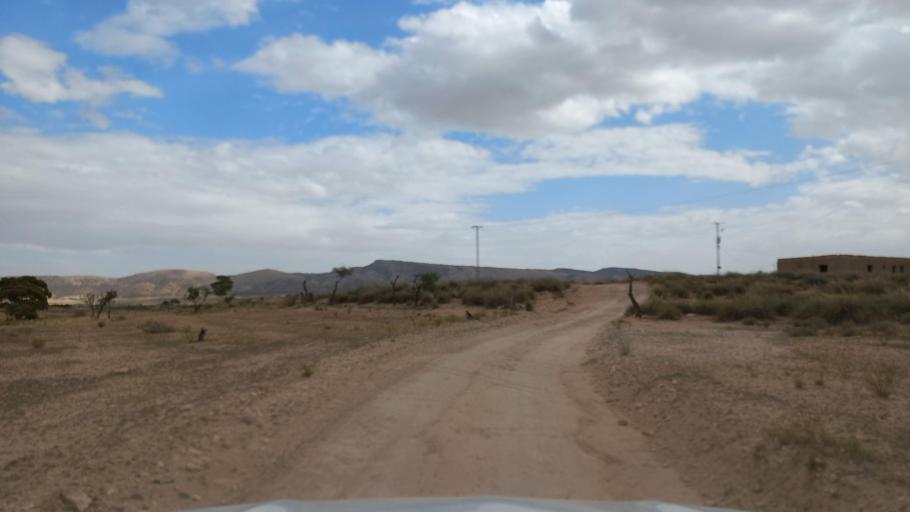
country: TN
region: Al Qasrayn
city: Sbiba
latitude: 35.3809
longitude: 9.1173
